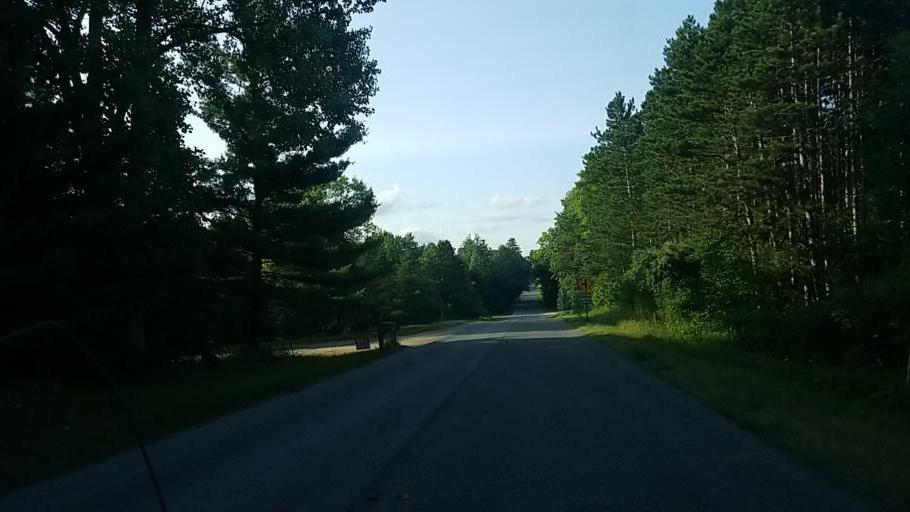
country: US
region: Michigan
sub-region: Montcalm County
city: Greenville
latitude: 43.1549
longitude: -85.3525
